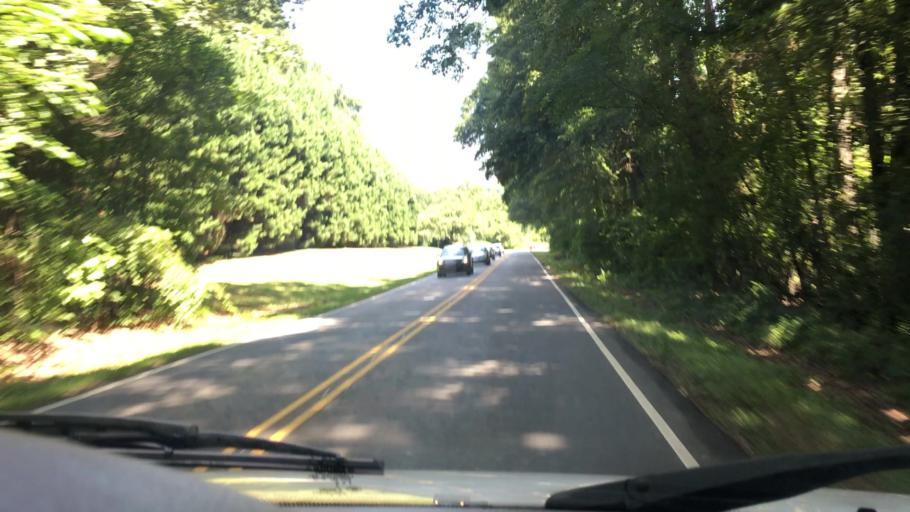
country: US
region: North Carolina
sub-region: Mecklenburg County
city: Huntersville
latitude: 35.3868
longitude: -80.9206
